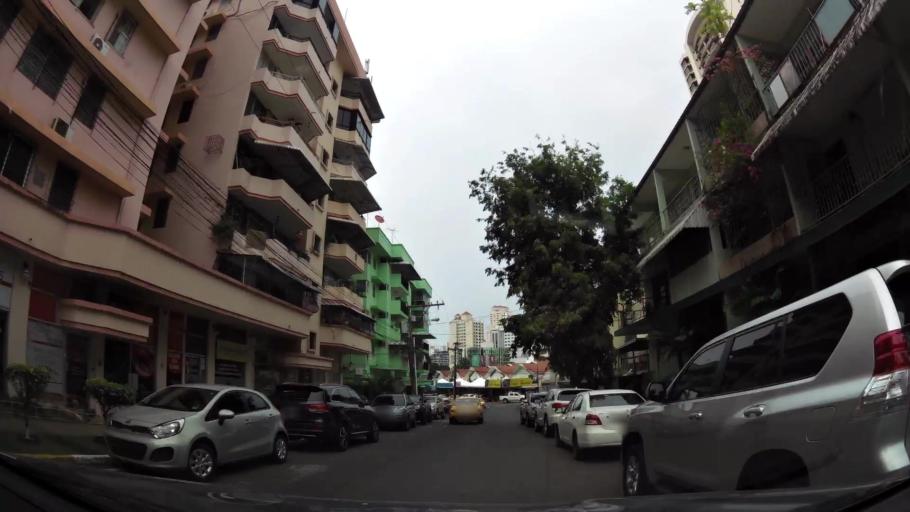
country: PA
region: Panama
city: Panama
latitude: 8.9873
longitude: -79.5218
